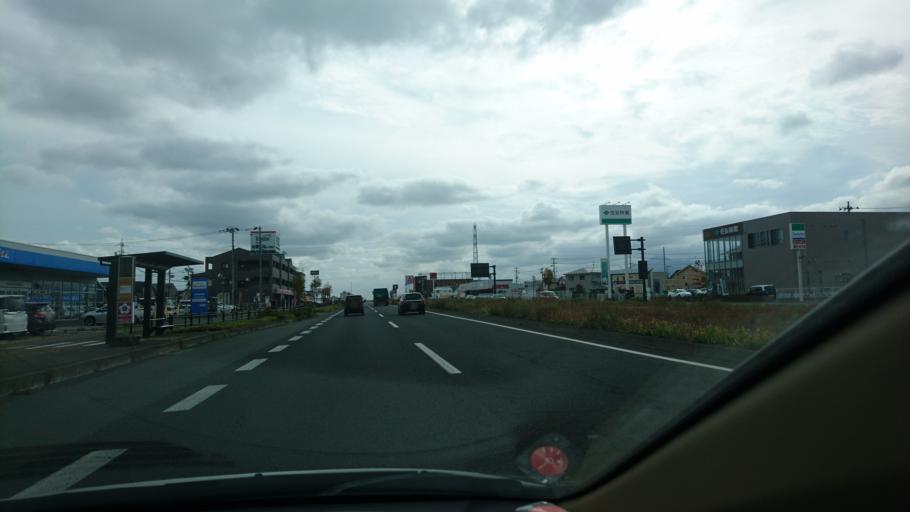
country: JP
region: Iwate
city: Morioka-shi
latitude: 39.6835
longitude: 141.1357
